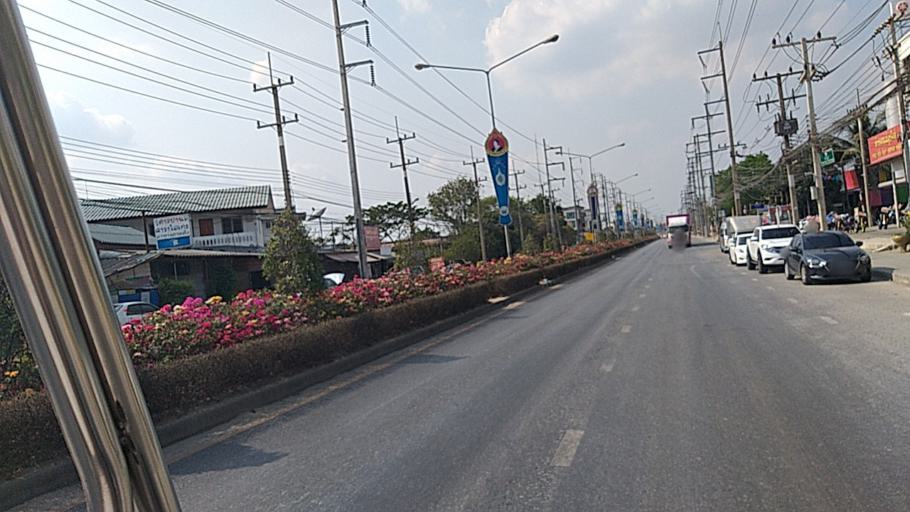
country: TH
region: Pathum Thani
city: Sam Khok
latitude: 14.0618
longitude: 100.5238
